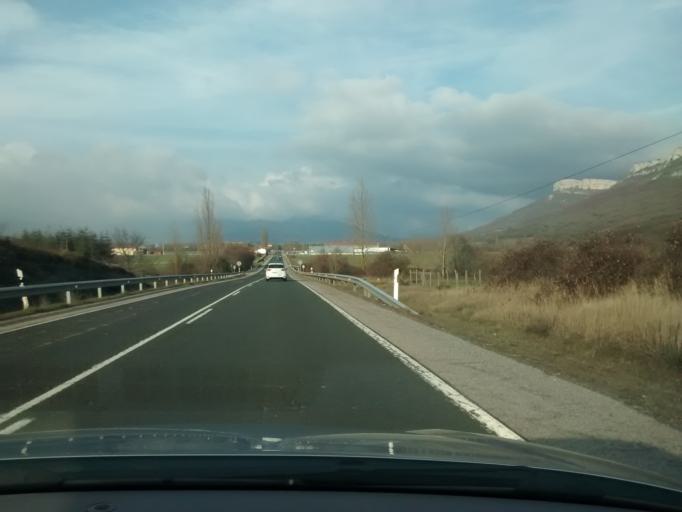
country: ES
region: Castille and Leon
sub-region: Provincia de Burgos
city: Espinosa de los Monteros
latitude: 43.0528
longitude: -3.4826
